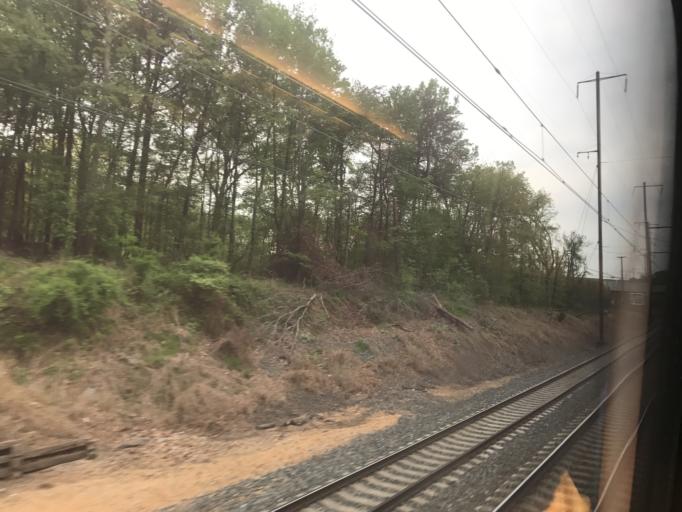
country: US
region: Maryland
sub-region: Howard County
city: Elkridge
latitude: 39.2280
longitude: -76.6925
